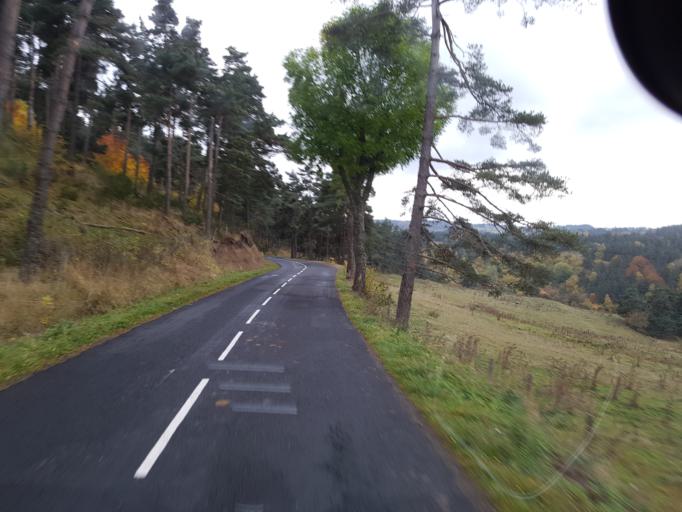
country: FR
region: Languedoc-Roussillon
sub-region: Departement de la Lozere
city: Langogne
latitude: 44.7196
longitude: 3.8149
